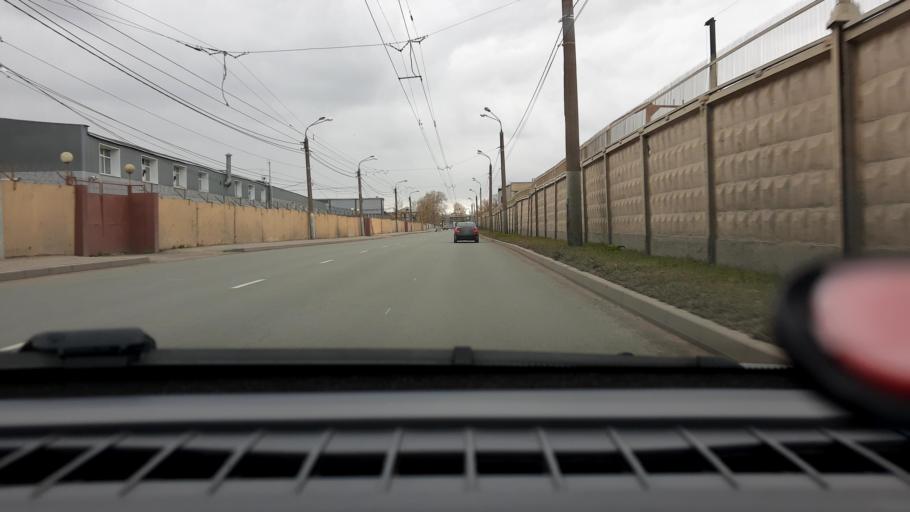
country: RU
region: Nizjnij Novgorod
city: Nizhniy Novgorod
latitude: 56.2392
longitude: 43.8932
